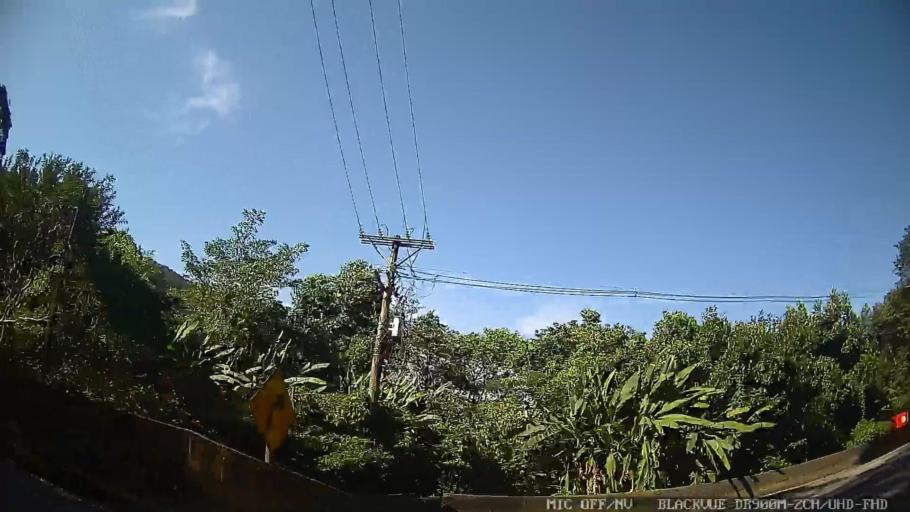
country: BR
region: Sao Paulo
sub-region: Cubatao
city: Cubatao
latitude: -23.8906
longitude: -46.4903
